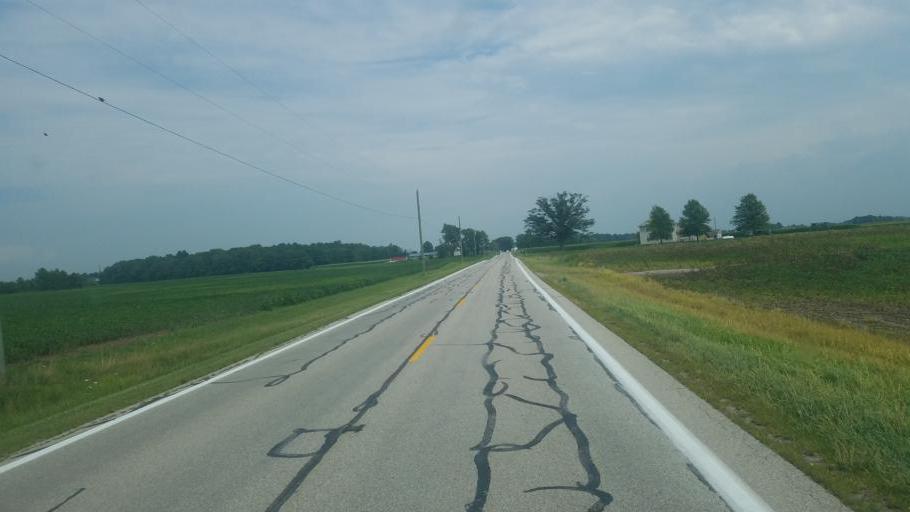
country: US
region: Ohio
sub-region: Union County
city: Richwood
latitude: 40.3504
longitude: -83.3667
